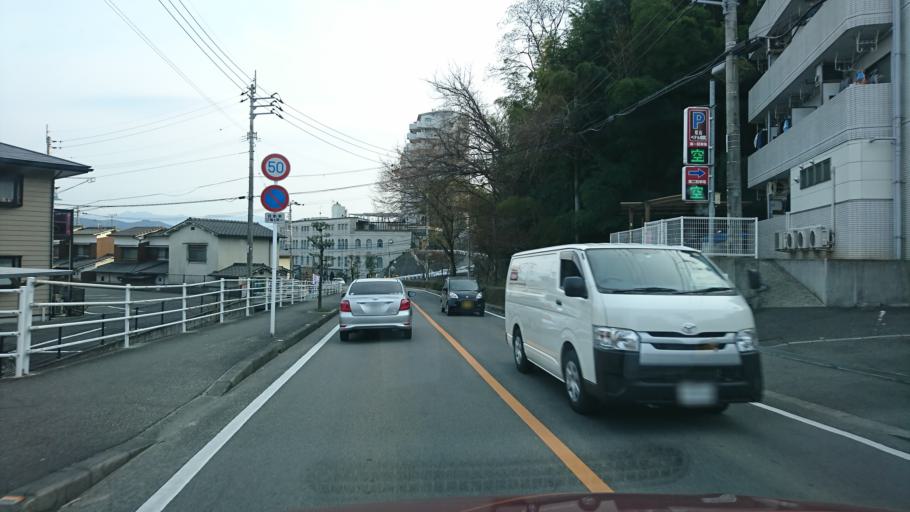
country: JP
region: Ehime
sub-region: Shikoku-chuo Shi
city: Matsuyama
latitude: 33.8634
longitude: 132.7739
